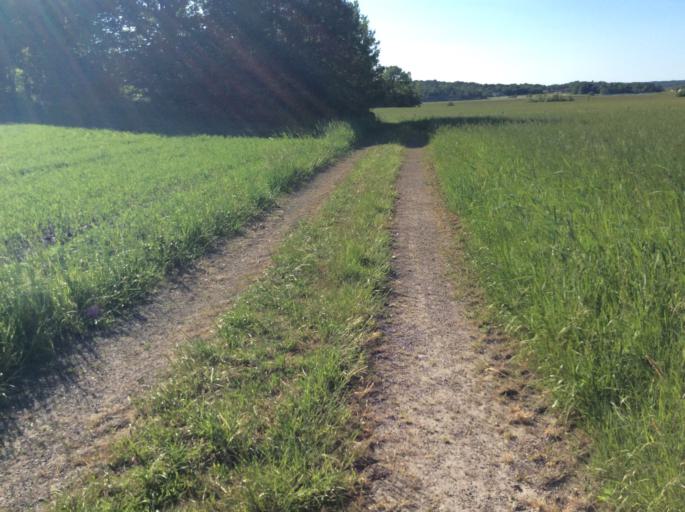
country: SE
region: Vaestra Goetaland
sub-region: Goteborg
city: Majorna
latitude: 57.7986
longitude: 11.8731
